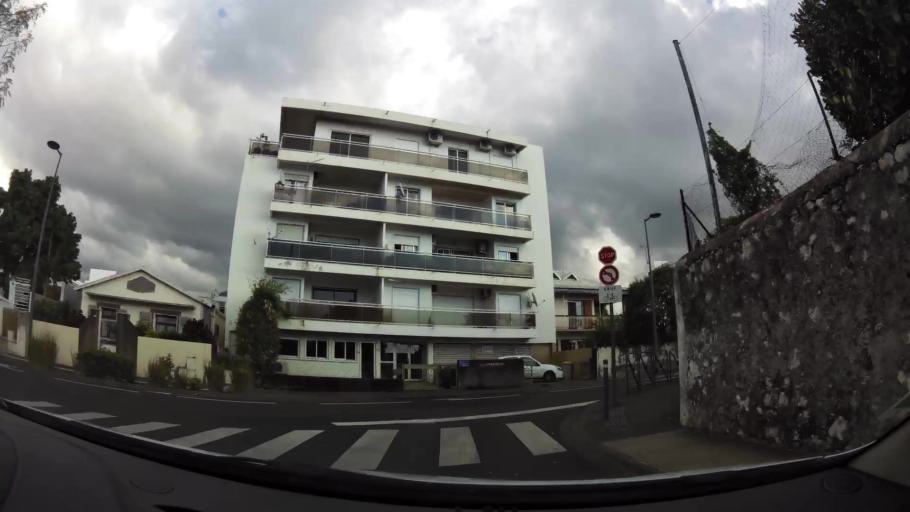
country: RE
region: Reunion
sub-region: Reunion
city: Saint-Denis
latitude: -20.8855
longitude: 55.4564
